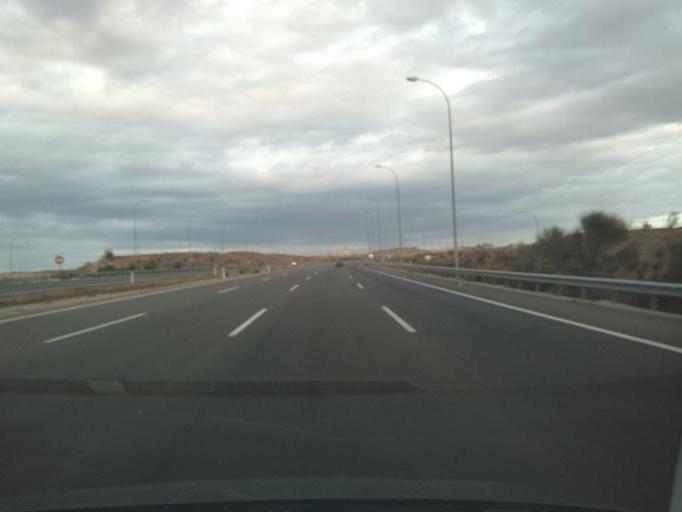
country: ES
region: Madrid
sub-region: Provincia de Madrid
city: Paracuellos de Jarama
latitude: 40.5427
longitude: -3.5403
